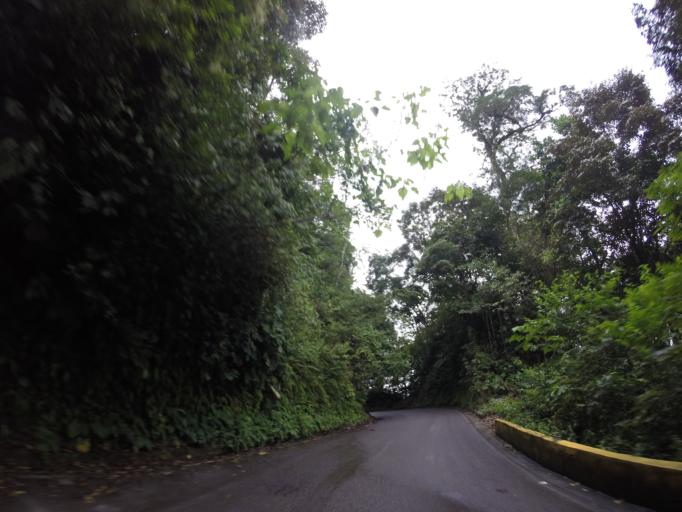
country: CO
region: Caldas
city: Victoria
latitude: 5.3238
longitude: -74.9275
